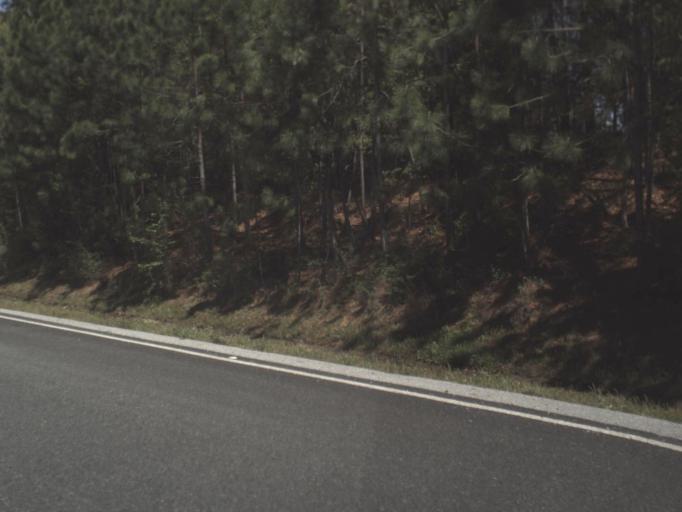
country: US
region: Florida
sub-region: Escambia County
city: Gonzalez
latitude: 30.5369
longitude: -87.3376
